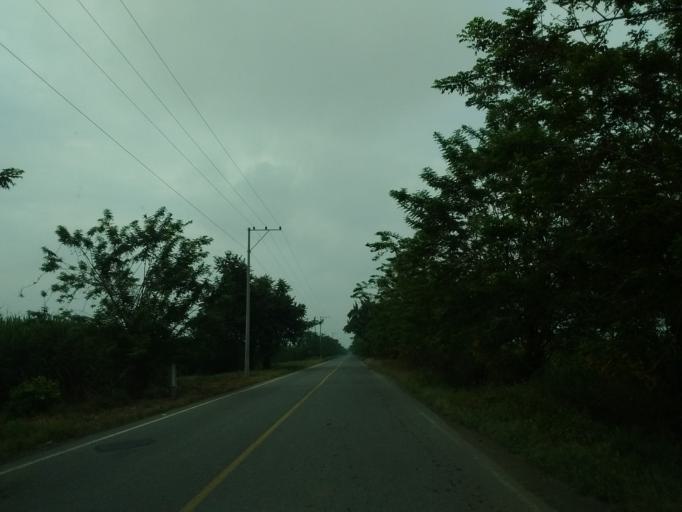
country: CO
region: Cauca
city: Padilla
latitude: 3.2275
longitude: -76.3408
